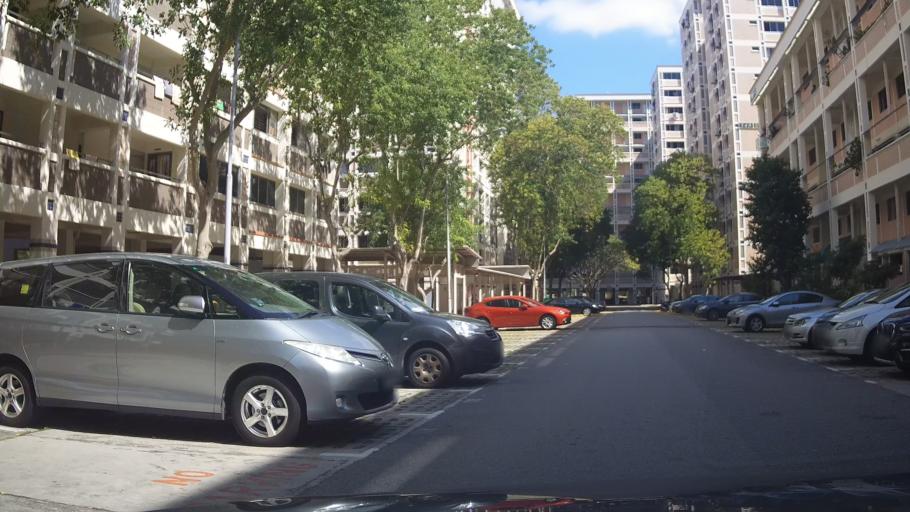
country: SG
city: Singapore
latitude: 1.3674
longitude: 103.9535
